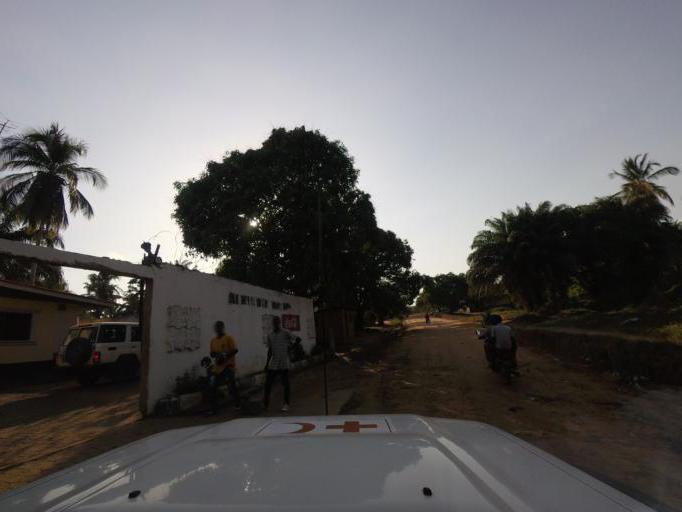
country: LR
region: Bong
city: Gbarnga
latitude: 7.0057
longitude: -9.4847
